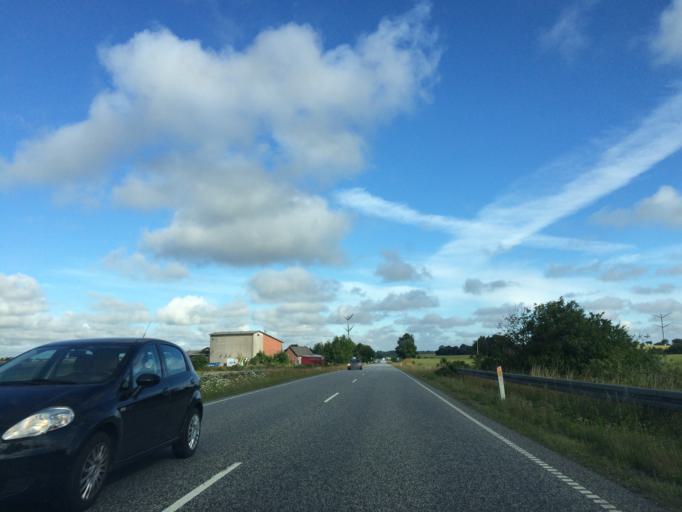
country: DK
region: Central Jutland
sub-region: Viborg Kommune
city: Bjerringbro
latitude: 56.3300
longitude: 9.5505
